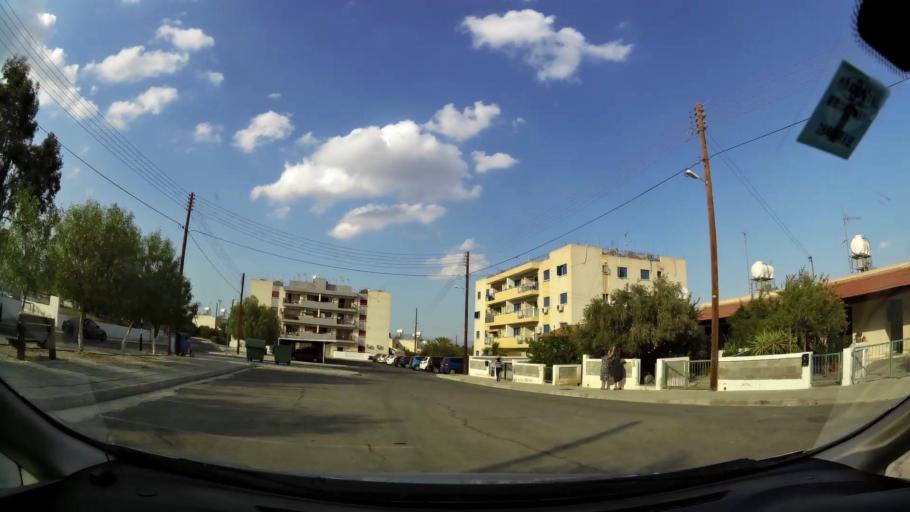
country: CY
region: Lefkosia
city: Kato Deftera
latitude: 35.1042
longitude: 33.2926
